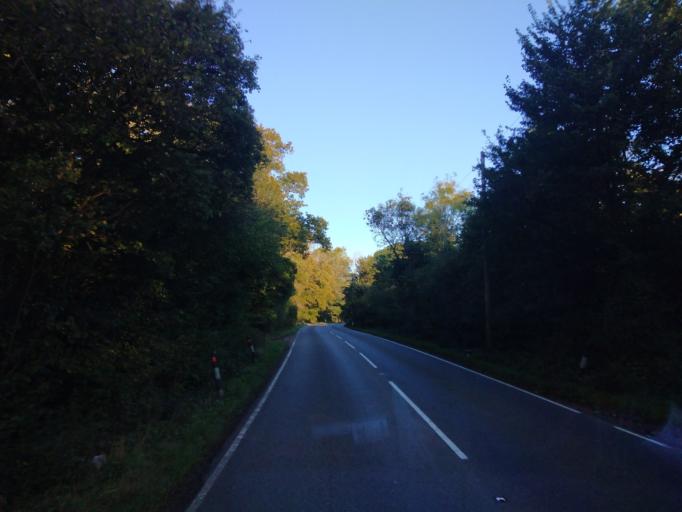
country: GB
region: England
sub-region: West Sussex
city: Goring-by-Sea
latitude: 50.8332
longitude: -0.4369
